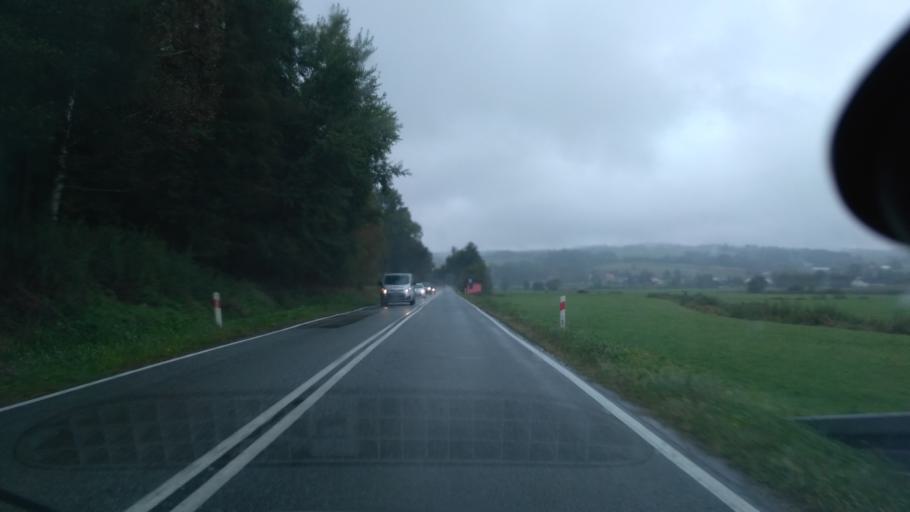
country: PL
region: Subcarpathian Voivodeship
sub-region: Powiat ropczycko-sedziszowski
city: Niedzwiada
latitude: 49.9808
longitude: 21.5594
